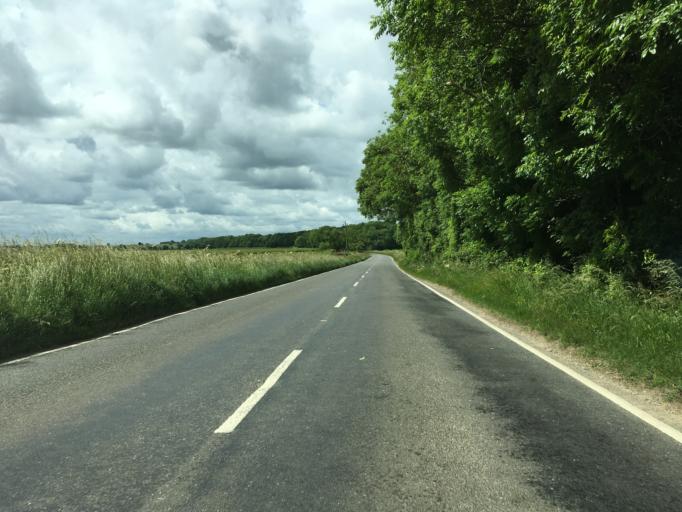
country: GB
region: England
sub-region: Oxfordshire
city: Chipping Norton
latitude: 51.9148
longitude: -1.5484
